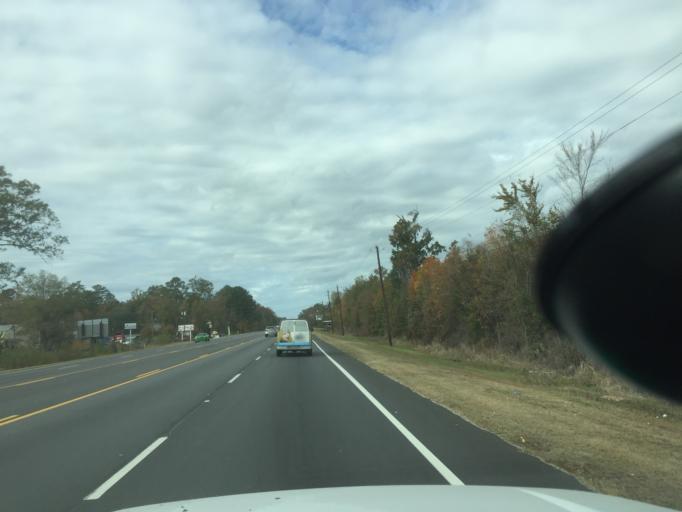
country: US
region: Georgia
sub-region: Chatham County
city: Garden City
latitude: 32.0904
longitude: -81.1861
